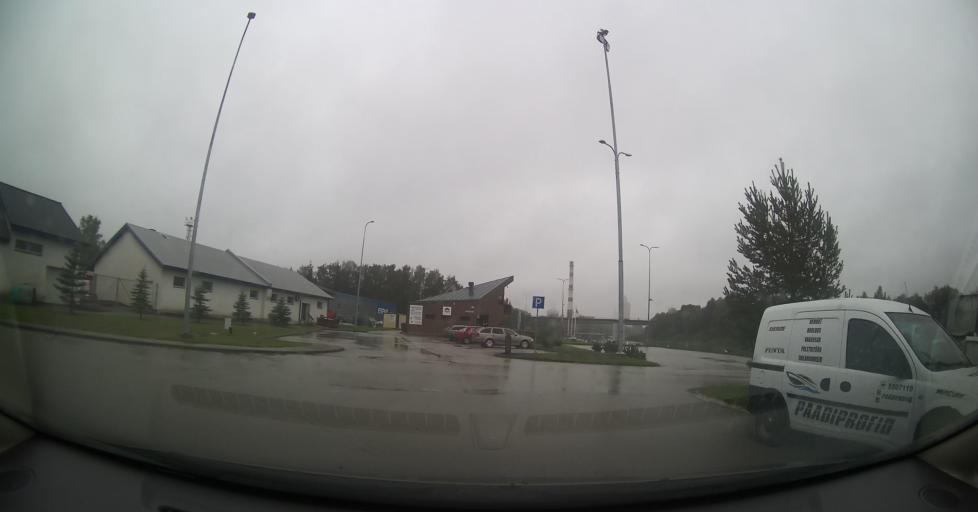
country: EE
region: Tartu
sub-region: Tartu linn
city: Tartu
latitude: 58.3688
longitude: 26.7456
